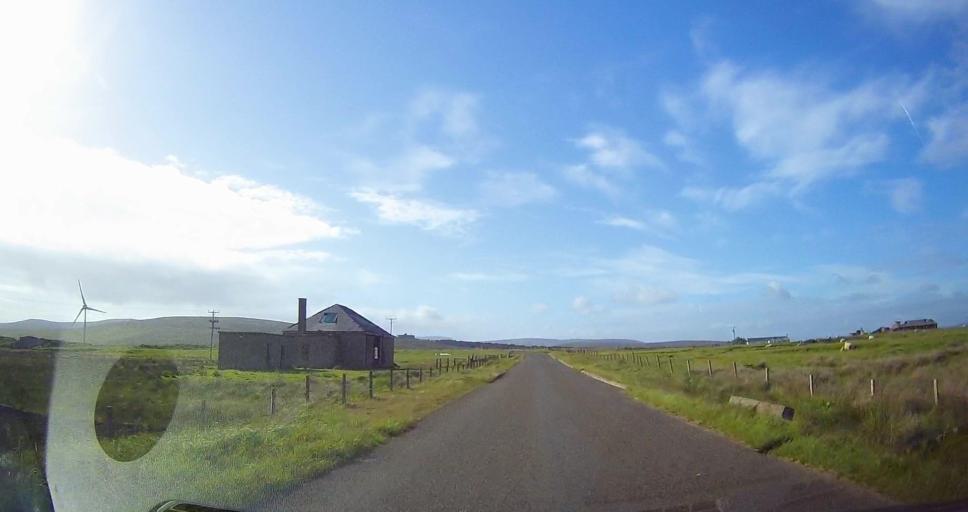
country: GB
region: Scotland
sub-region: Orkney Islands
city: Stromness
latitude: 58.8214
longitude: -3.2049
